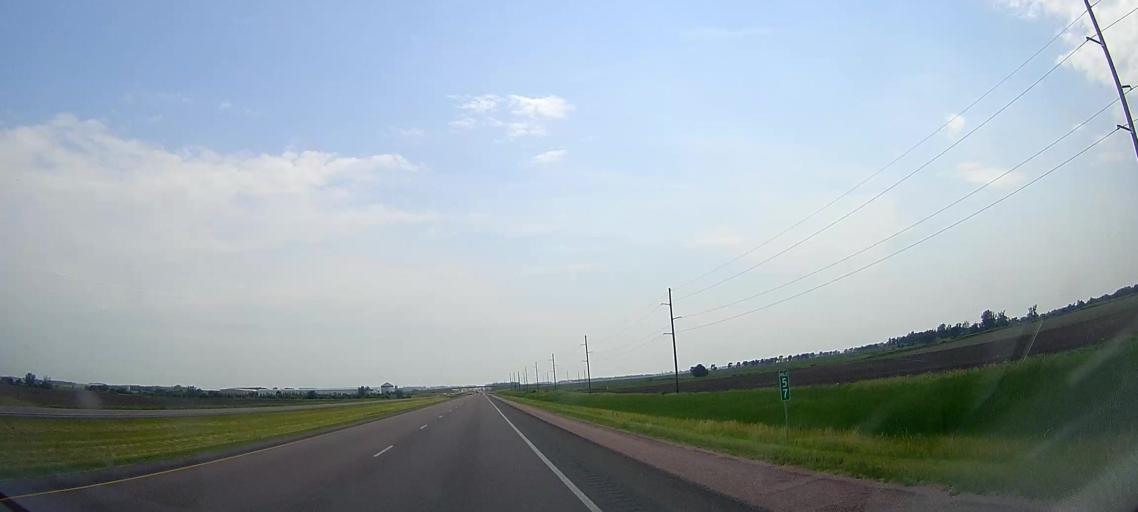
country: US
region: South Dakota
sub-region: Union County
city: Beresford
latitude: 43.2237
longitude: -96.7962
